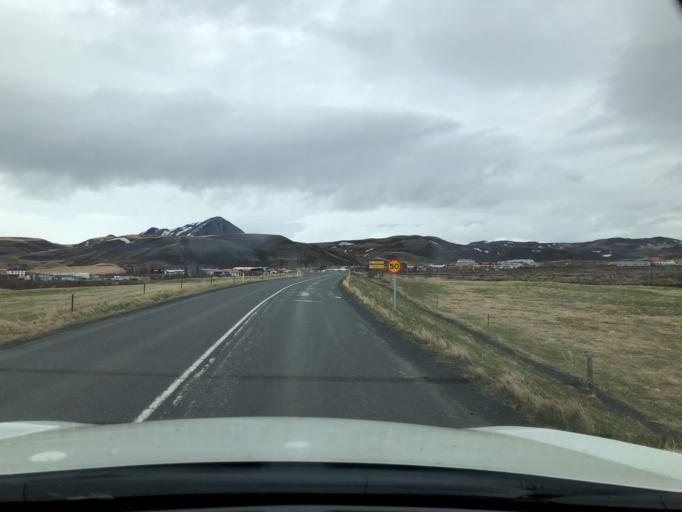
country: IS
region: Northeast
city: Laugar
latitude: 65.6371
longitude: -16.9139
